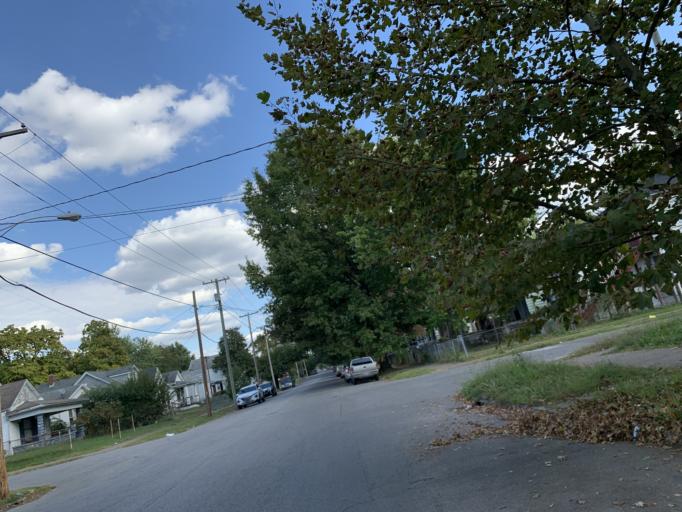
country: US
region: Kentucky
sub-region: Jefferson County
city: Louisville
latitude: 38.2445
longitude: -85.7939
